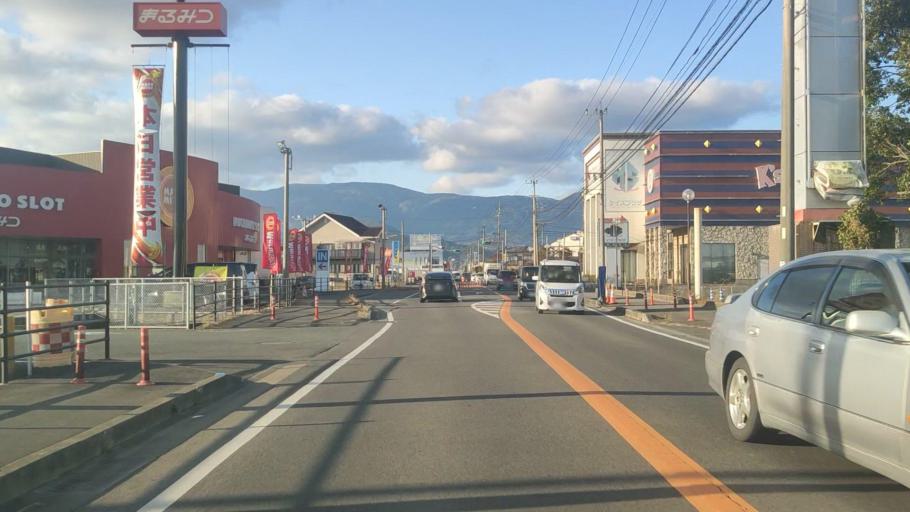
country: JP
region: Saga Prefecture
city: Saga-shi
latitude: 33.2787
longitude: 130.2140
